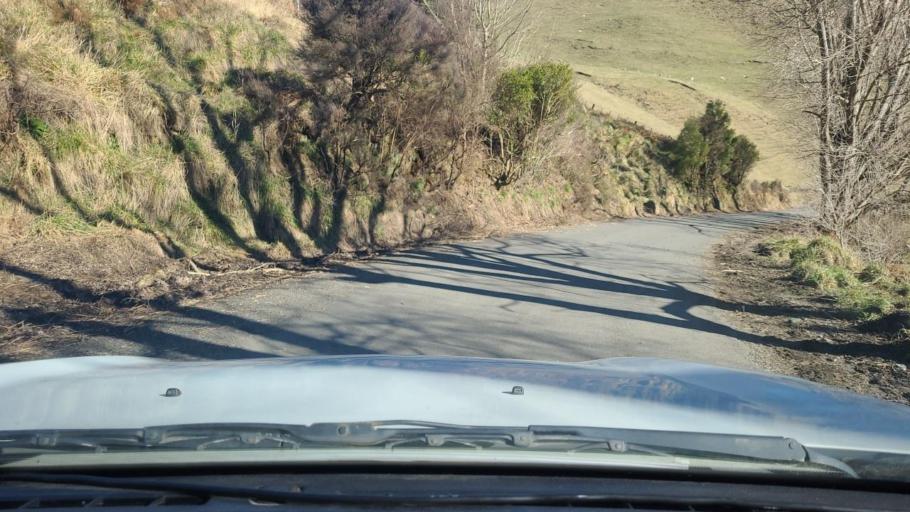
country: NZ
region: Hawke's Bay
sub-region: Napier City
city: Taradale
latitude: -39.2376
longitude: 176.4984
